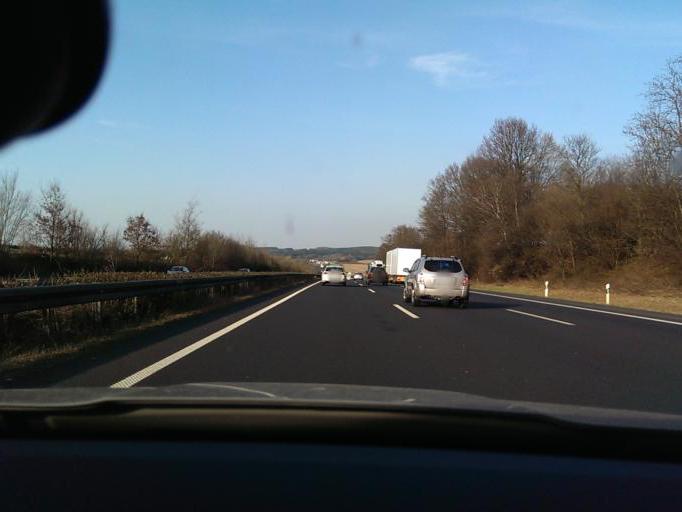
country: DE
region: Hesse
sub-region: Regierungsbezirk Kassel
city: Fuldatal
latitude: 51.3390
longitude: 9.5921
